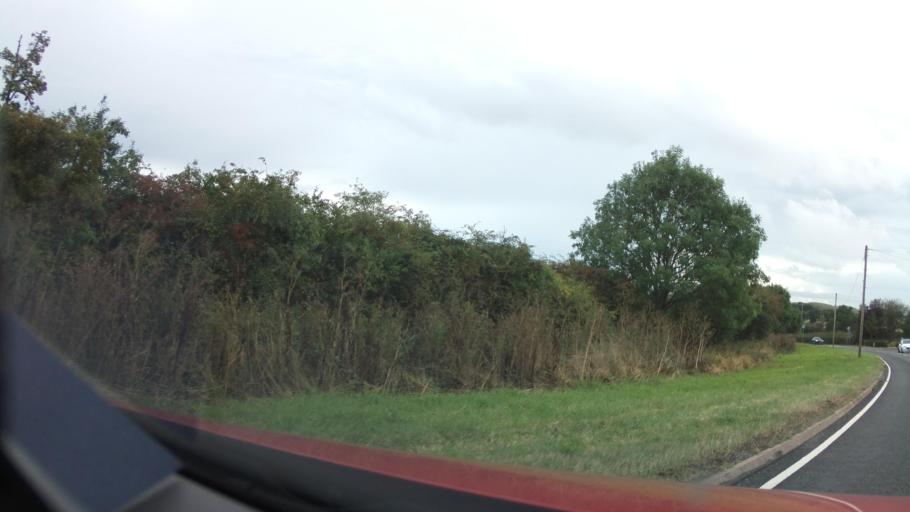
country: GB
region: England
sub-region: Worcestershire
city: Droitwich
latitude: 52.3108
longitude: -2.1781
